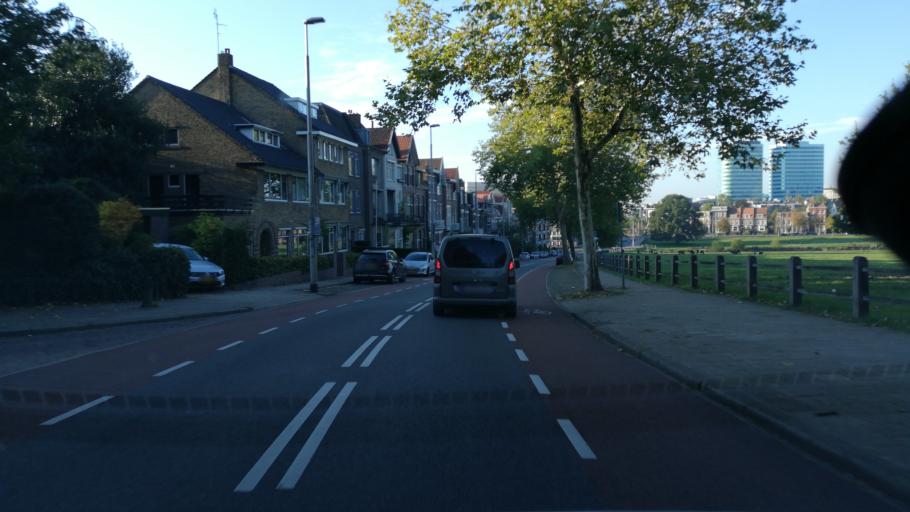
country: NL
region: Gelderland
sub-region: Gemeente Arnhem
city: Arnhem
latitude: 51.9883
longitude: 5.9079
